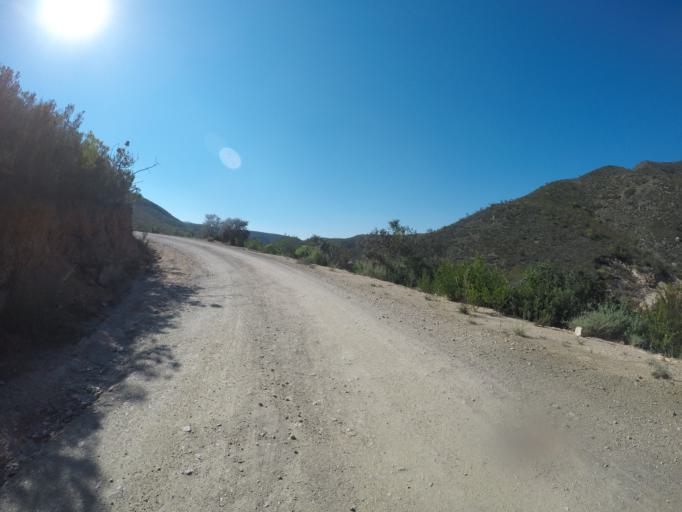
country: ZA
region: Eastern Cape
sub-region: Cacadu District Municipality
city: Kareedouw
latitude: -33.6532
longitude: 24.4987
